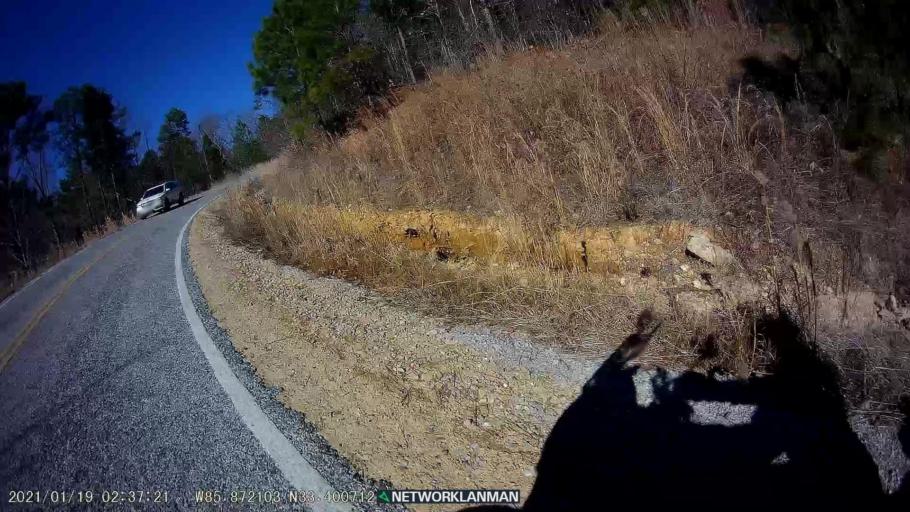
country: US
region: Alabama
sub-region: Clay County
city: Ashland
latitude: 33.4008
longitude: -85.8722
